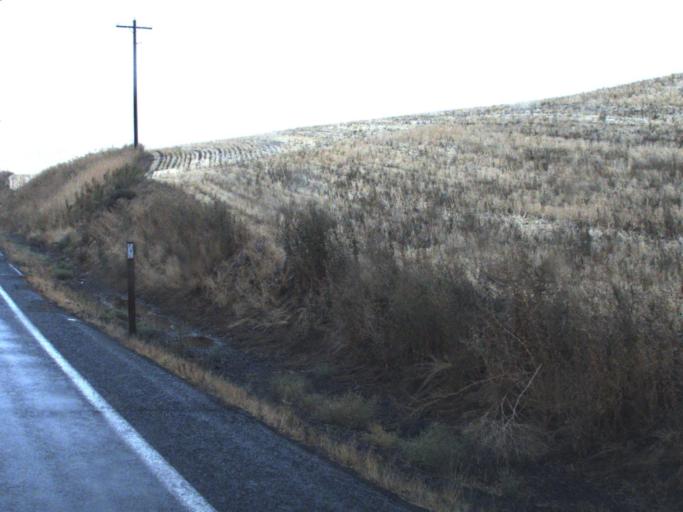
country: US
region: Washington
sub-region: Whitman County
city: Colfax
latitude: 47.1106
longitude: -117.6371
